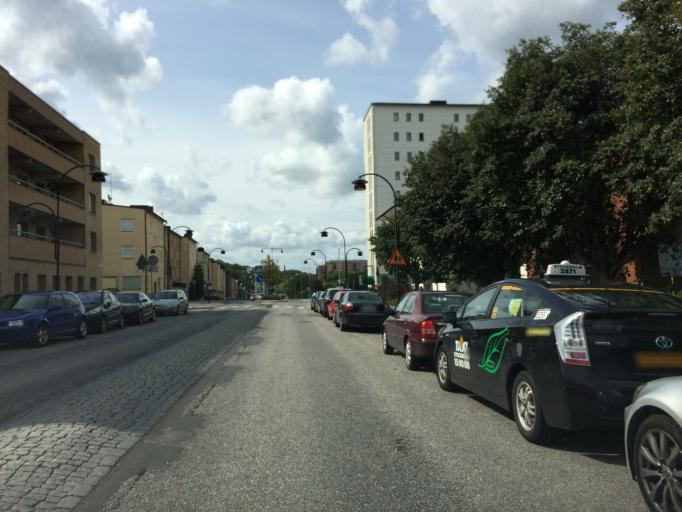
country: SE
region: Stockholm
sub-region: Solna Kommun
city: Solna
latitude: 59.3051
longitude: 17.9905
